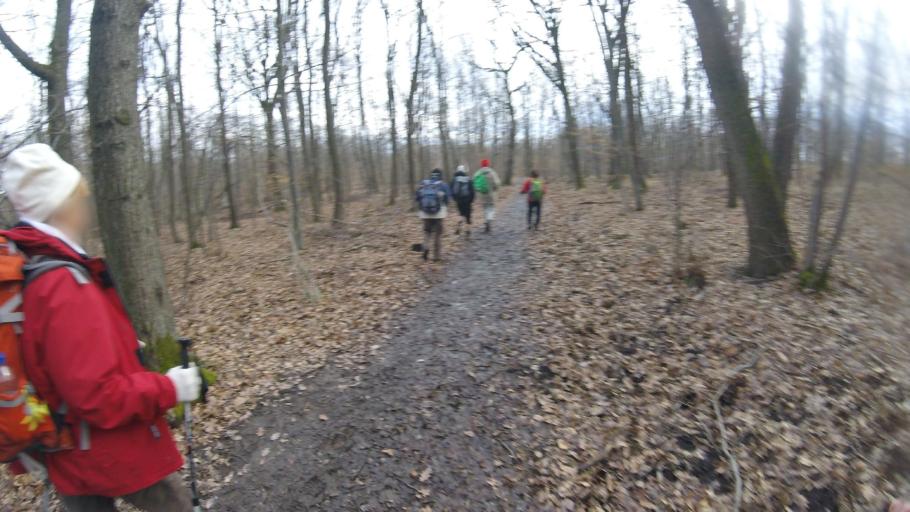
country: HU
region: Pest
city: Nagykovacsi
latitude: 47.6887
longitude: 18.9889
